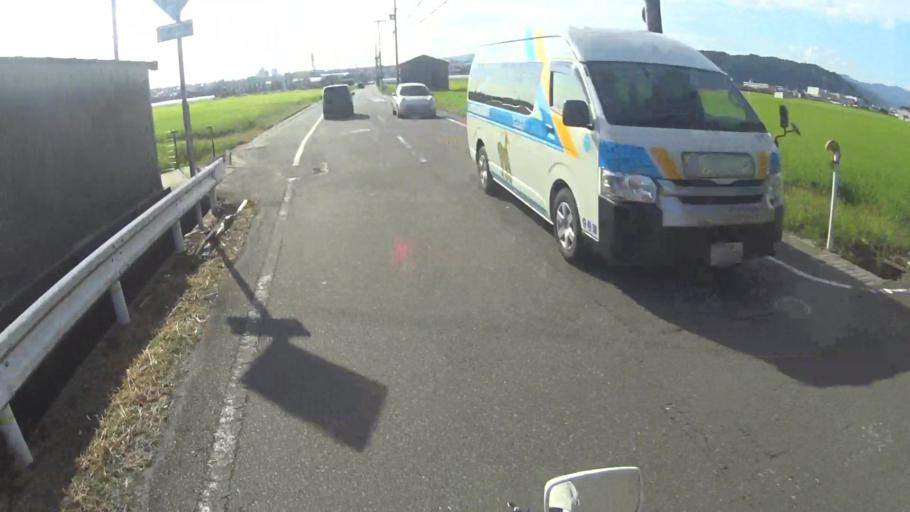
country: JP
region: Kyoto
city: Yawata
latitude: 34.8662
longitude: 135.7177
